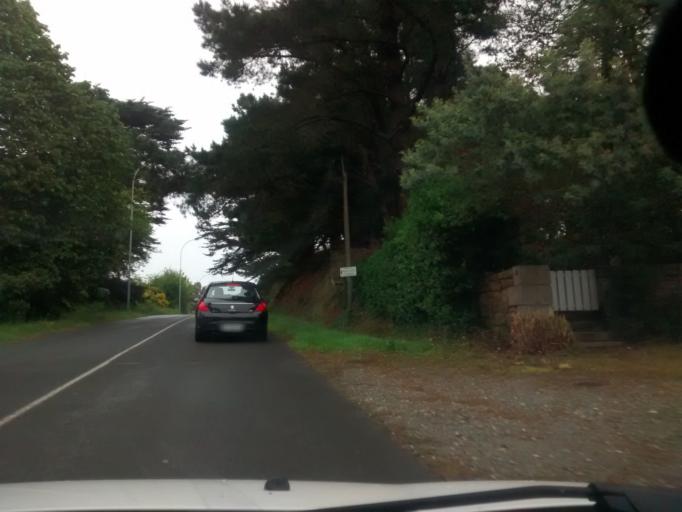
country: FR
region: Brittany
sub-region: Departement des Cotes-d'Armor
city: Trevou-Treguignec
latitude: 48.8322
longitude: -3.3163
